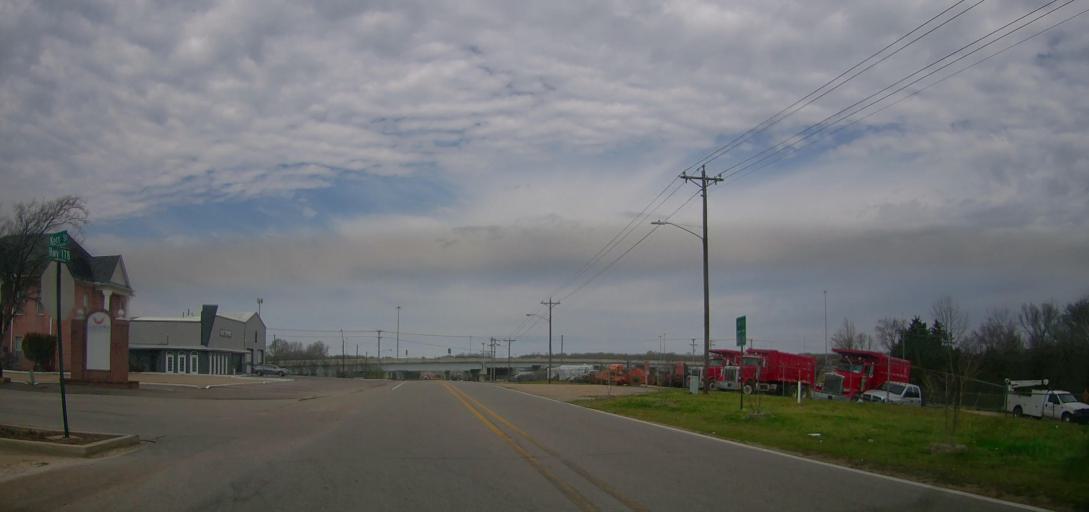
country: US
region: Mississippi
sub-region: De Soto County
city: Olive Branch
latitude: 34.9647
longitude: -89.8287
